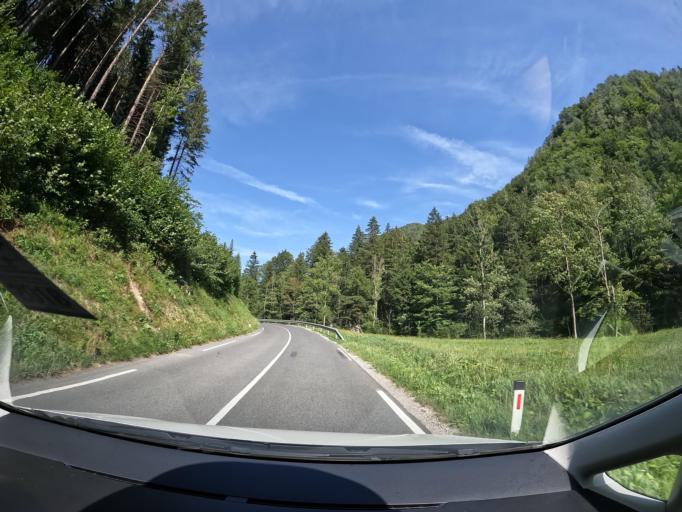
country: SI
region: Zirovnica
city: Zirovnica
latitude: 46.4429
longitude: 14.1777
